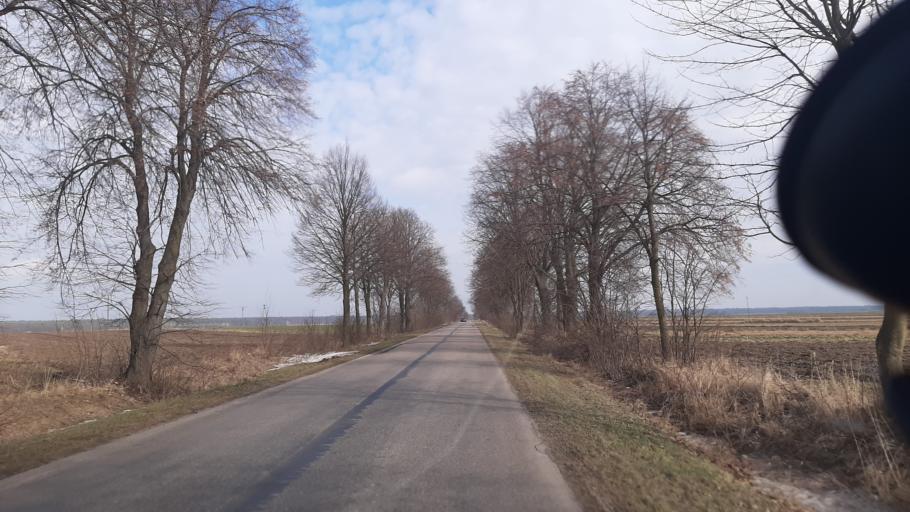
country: PL
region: Lublin Voivodeship
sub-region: Powiat lubartowski
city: Wola Sernicka
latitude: 51.4581
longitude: 22.6941
